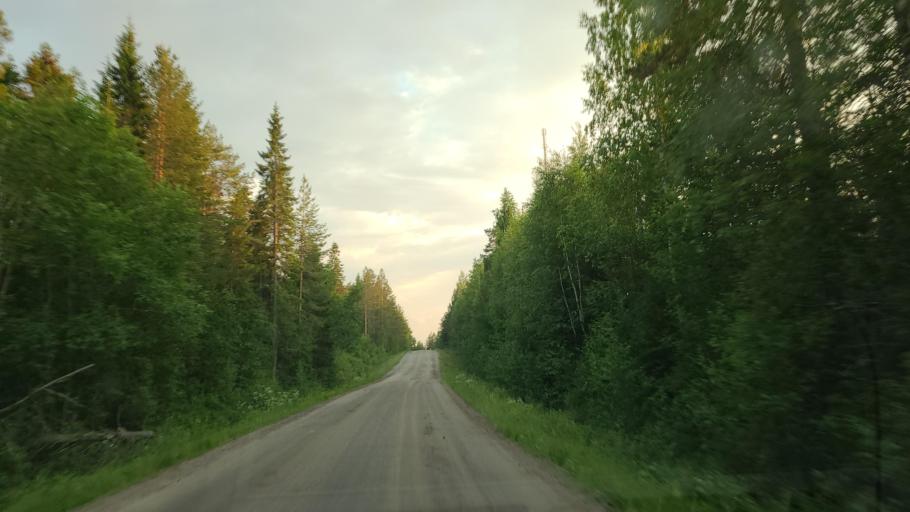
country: SE
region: Vaesterbotten
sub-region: Robertsfors Kommun
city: Robertsfors
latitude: 64.0708
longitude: 20.8791
